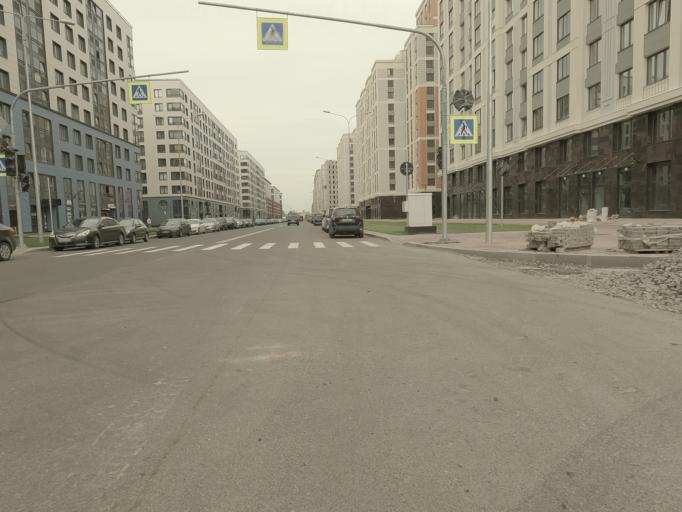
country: RU
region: St.-Petersburg
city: Admiralteisky
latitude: 59.8988
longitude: 30.3121
